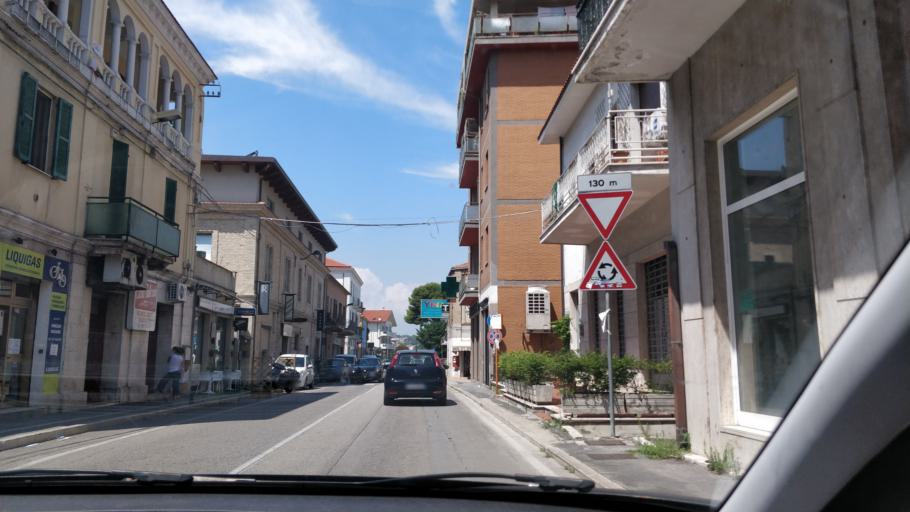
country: IT
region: Abruzzo
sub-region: Provincia di Chieti
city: Francavilla al Mare
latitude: 42.4206
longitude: 14.2880
